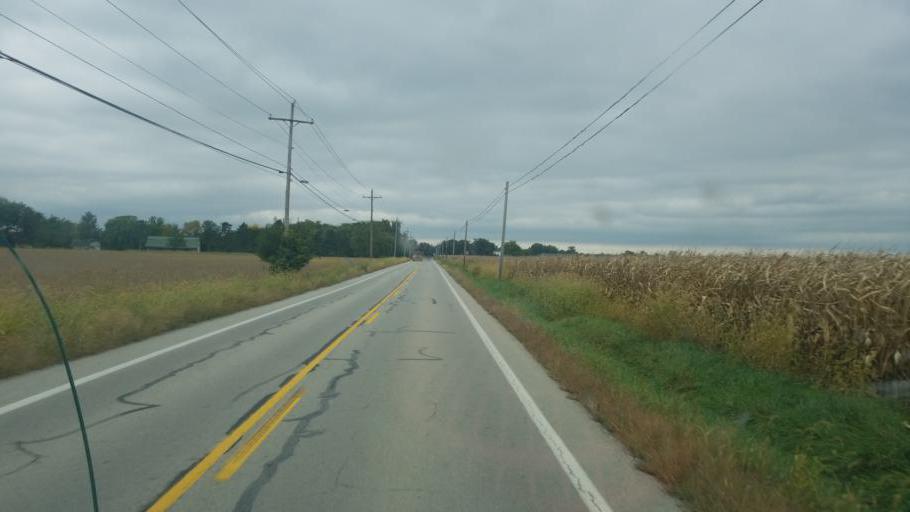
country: US
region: Ohio
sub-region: Lucas County
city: Waterville
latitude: 41.4858
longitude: -83.7112
